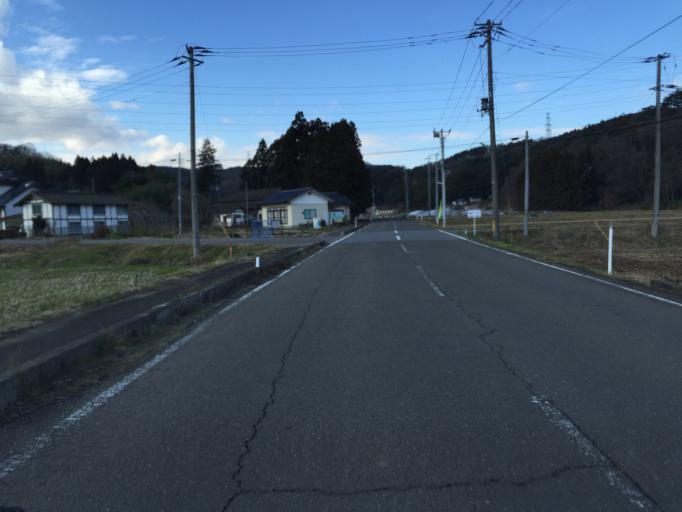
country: JP
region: Fukushima
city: Nihommatsu
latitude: 37.6682
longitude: 140.4174
